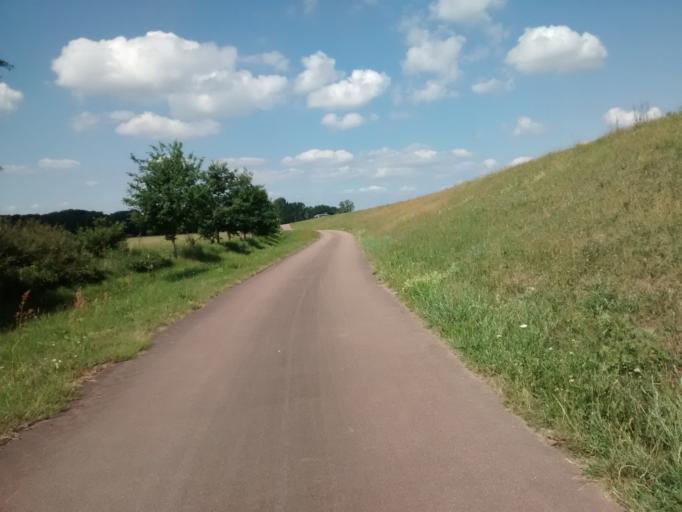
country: DE
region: Saxony-Anhalt
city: Bergwitz
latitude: 51.8536
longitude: 12.5652
